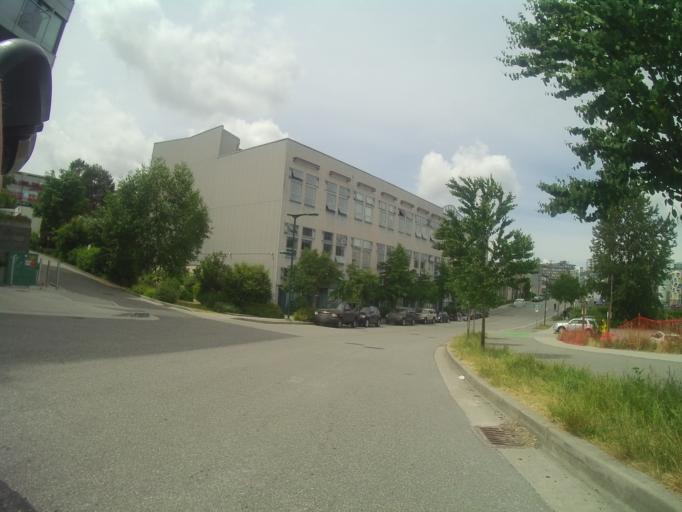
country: CA
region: British Columbia
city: Vancouver
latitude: 49.2677
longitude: -123.0960
